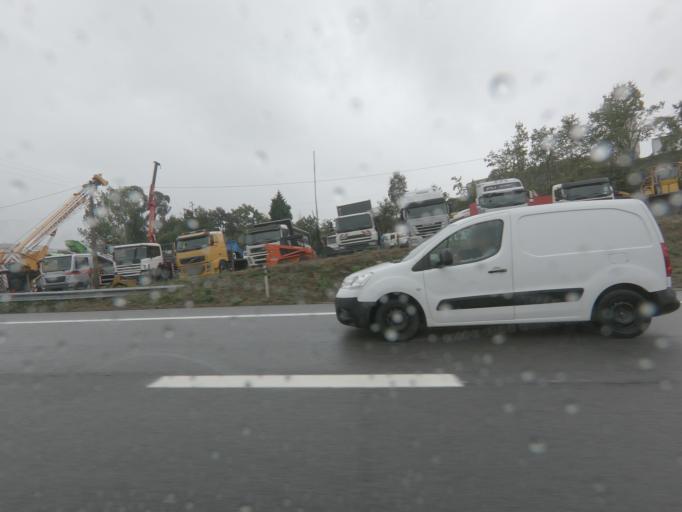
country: PT
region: Porto
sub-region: Penafiel
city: Penafiel
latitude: 41.2018
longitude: -8.3060
